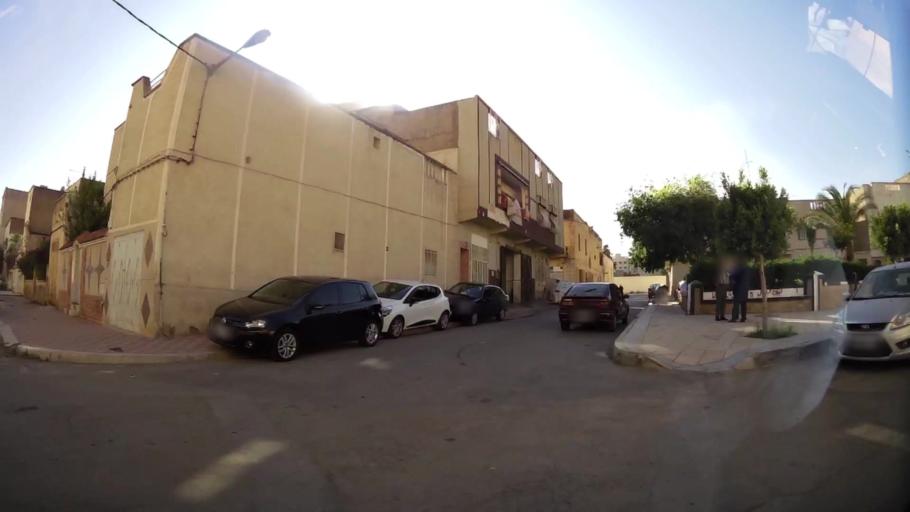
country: MA
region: Oriental
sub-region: Oujda-Angad
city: Oujda
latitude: 34.6879
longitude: -1.9120
